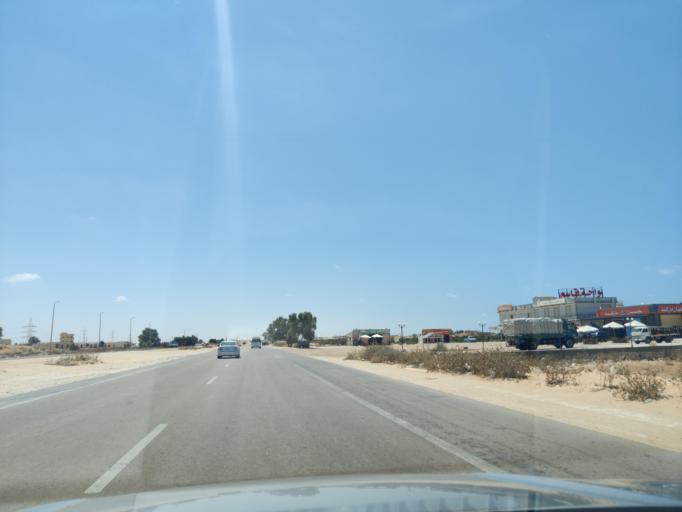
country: EG
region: Muhafazat Matruh
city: Al `Alamayn
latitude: 31.0696
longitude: 28.1287
